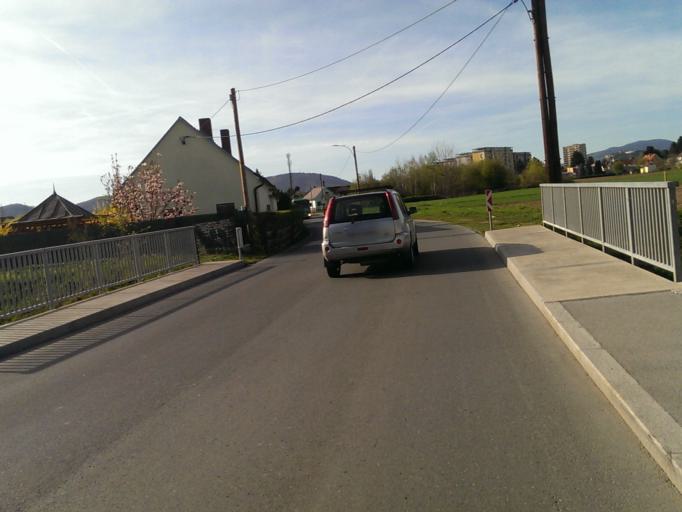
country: AT
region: Styria
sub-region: Politischer Bezirk Graz-Umgebung
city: Feldkirchen bei Graz
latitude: 47.0397
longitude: 15.4527
